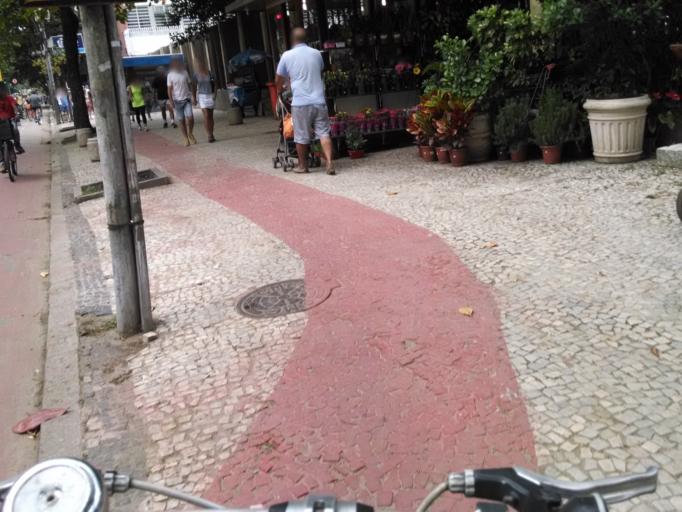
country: BR
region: Rio de Janeiro
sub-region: Rio De Janeiro
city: Rio de Janeiro
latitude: -22.9873
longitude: -43.1926
